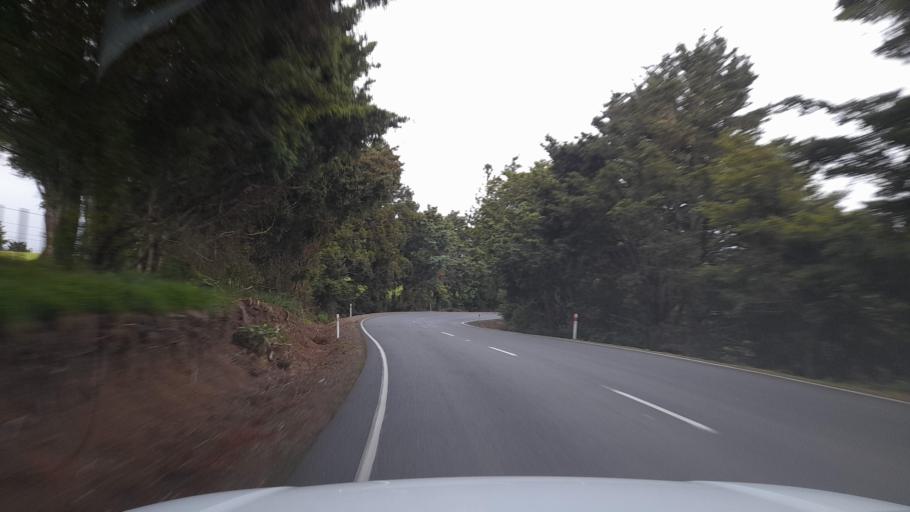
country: NZ
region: Northland
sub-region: Far North District
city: Waimate North
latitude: -35.5862
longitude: 173.8419
